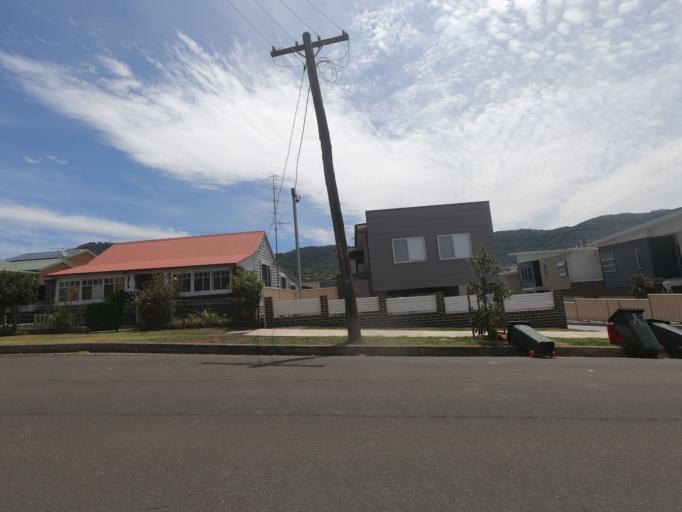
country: AU
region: New South Wales
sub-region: Wollongong
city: Mount Ousley
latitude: -34.3914
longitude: 150.8814
